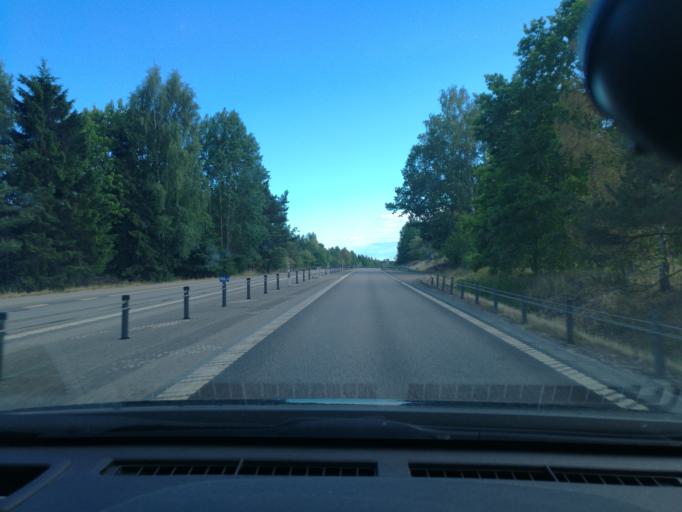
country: SE
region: Kalmar
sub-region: Oskarshamns Kommun
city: Oskarshamn
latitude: 57.2943
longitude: 16.4591
